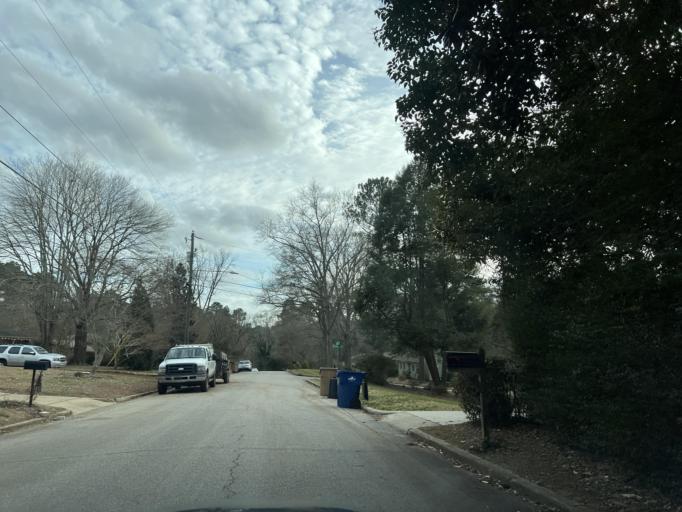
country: US
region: North Carolina
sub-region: Wake County
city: West Raleigh
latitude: 35.7743
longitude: -78.7049
